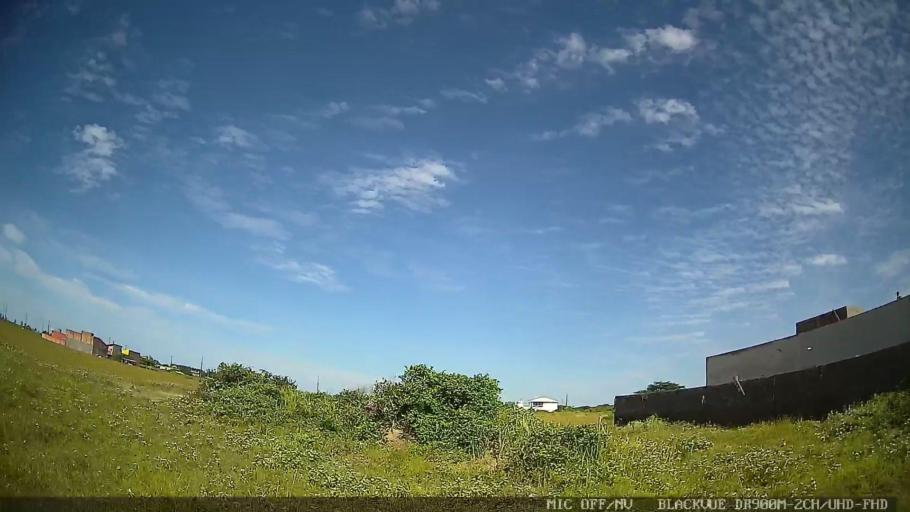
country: BR
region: Sao Paulo
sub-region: Iguape
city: Iguape
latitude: -24.7742
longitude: -47.5941
